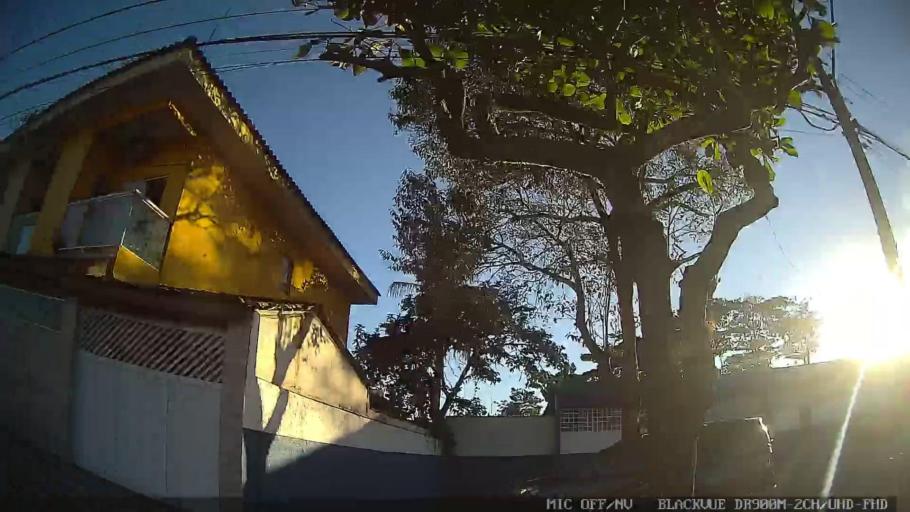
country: BR
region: Sao Paulo
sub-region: Guaruja
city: Guaruja
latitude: -23.9646
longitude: -46.2751
